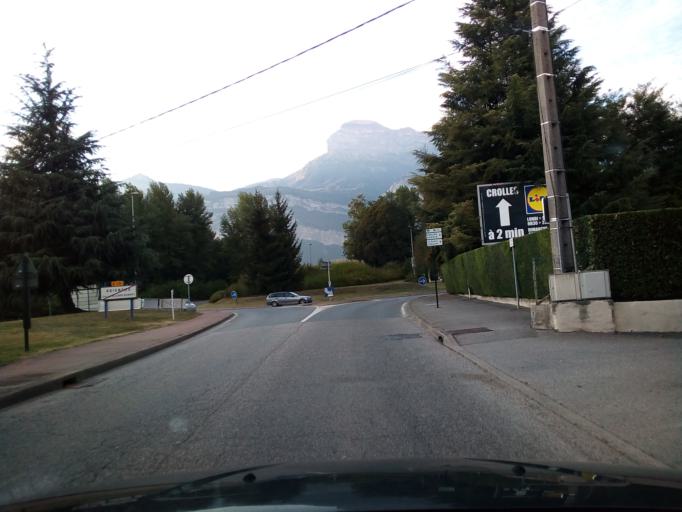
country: FR
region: Rhone-Alpes
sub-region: Departement de l'Isere
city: Froges
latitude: 45.2639
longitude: 5.9009
